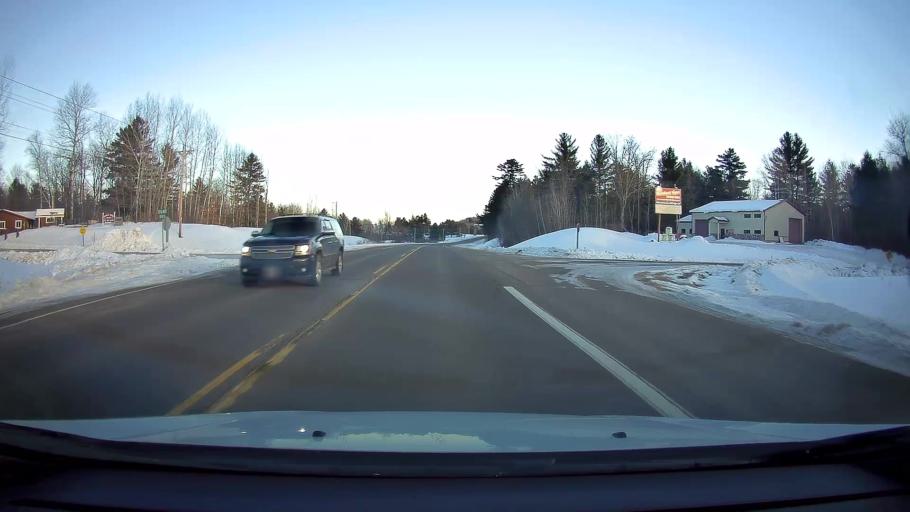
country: US
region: Wisconsin
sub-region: Barron County
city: Cumberland
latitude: 45.5961
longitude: -92.0177
